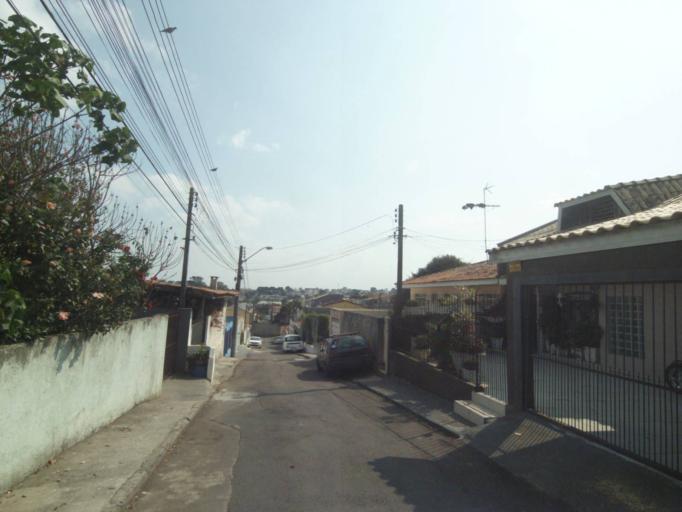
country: BR
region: Parana
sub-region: Sao Jose Dos Pinhais
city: Sao Jose dos Pinhais
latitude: -25.5221
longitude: -49.2451
